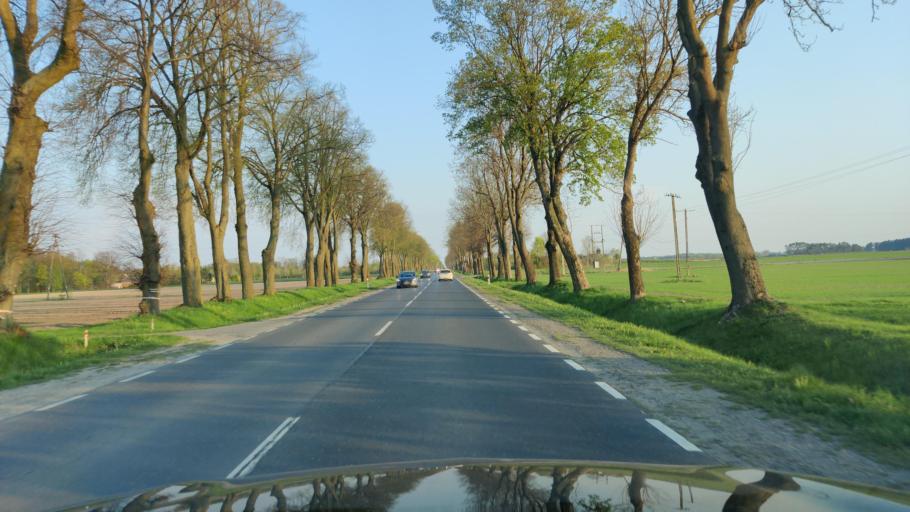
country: PL
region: Masovian Voivodeship
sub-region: Powiat pultuski
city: Pultusk
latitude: 52.6377
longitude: 21.0944
